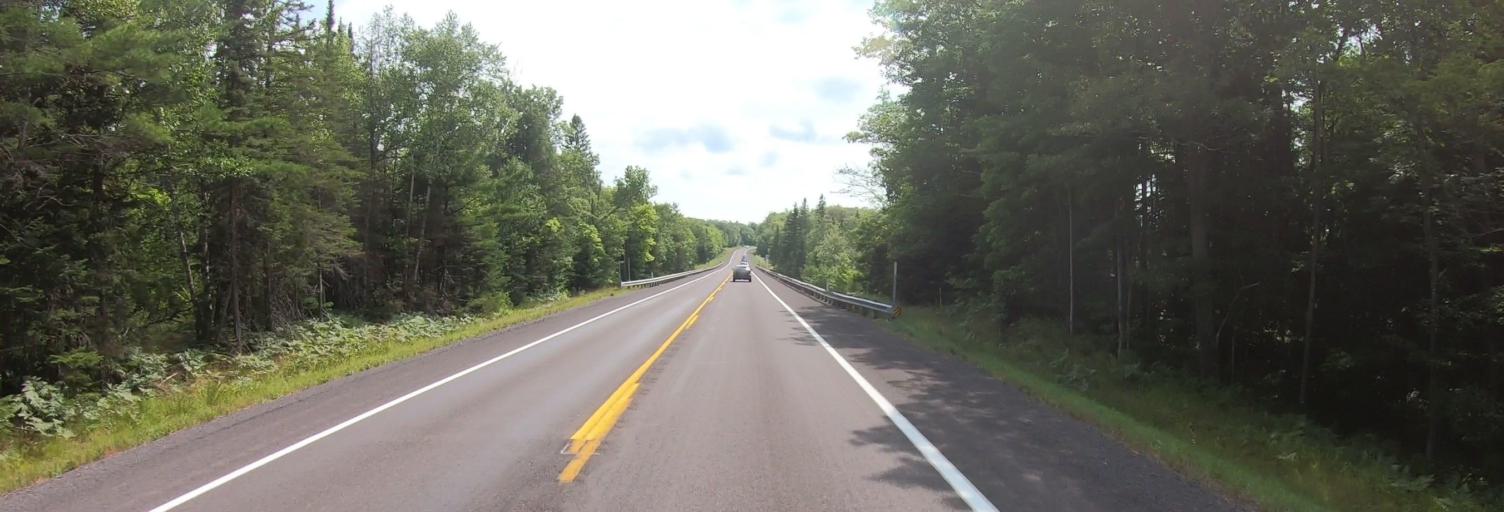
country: US
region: Michigan
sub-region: Houghton County
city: Hancock
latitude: 46.9566
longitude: -88.7794
